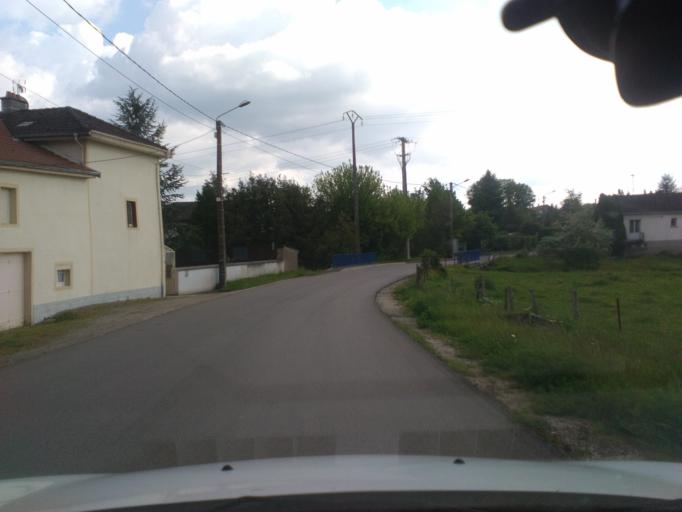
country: FR
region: Lorraine
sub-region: Departement des Vosges
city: Mirecourt
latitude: 48.3061
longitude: 6.1433
